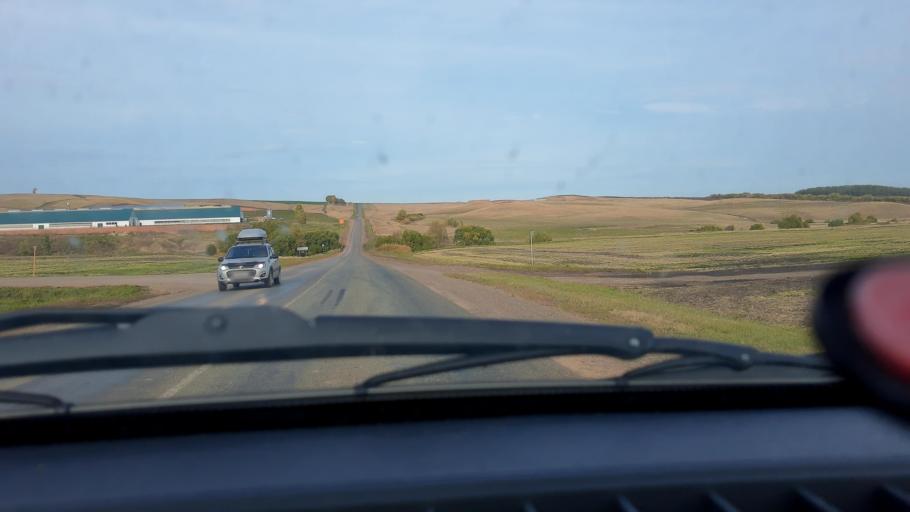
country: RU
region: Bashkortostan
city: Chekmagush
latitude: 55.0589
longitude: 54.6252
